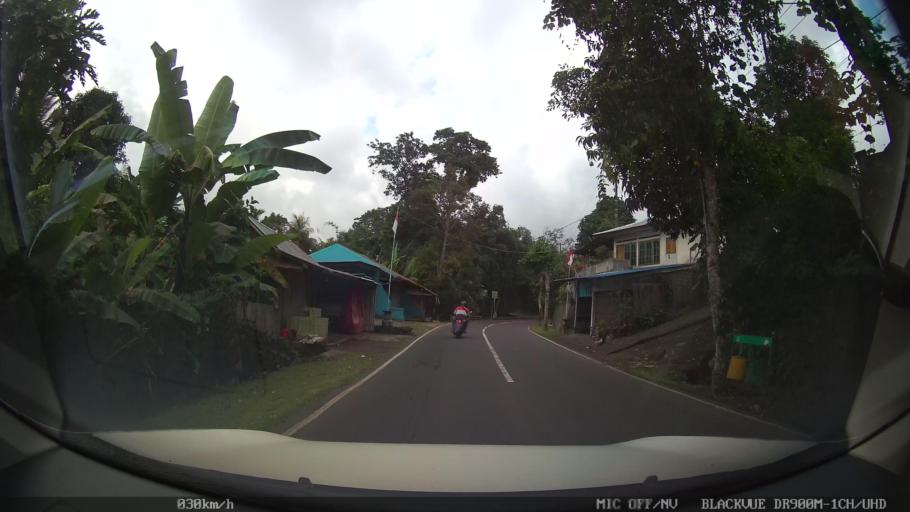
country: ID
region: Bali
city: Petang
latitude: -8.3835
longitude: 115.2195
